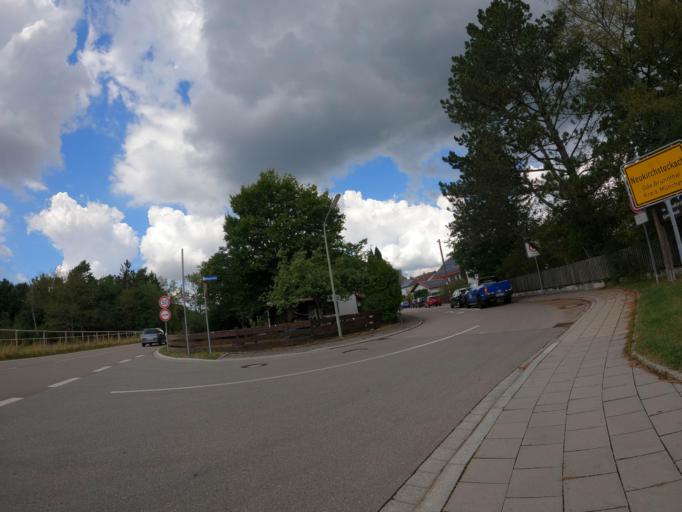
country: DE
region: Bavaria
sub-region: Upper Bavaria
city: Brunnthal
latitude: 48.0327
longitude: 11.6772
